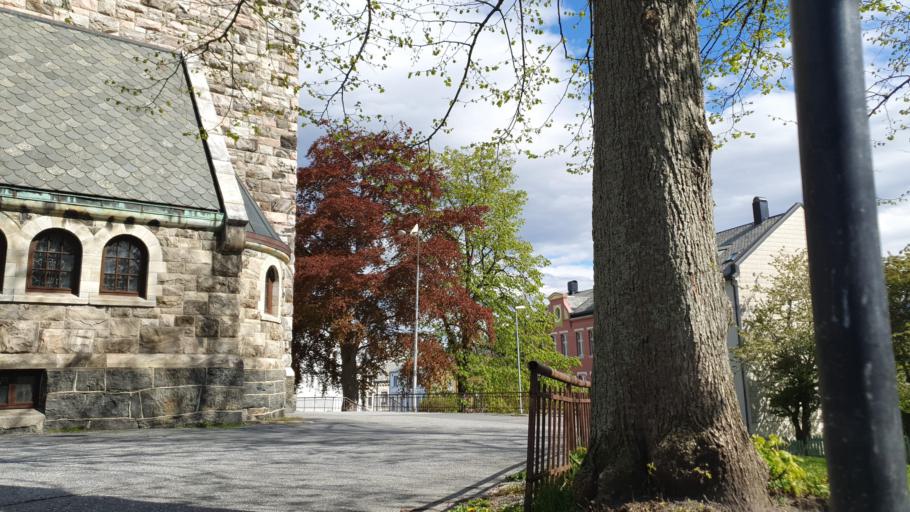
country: NO
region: More og Romsdal
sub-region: Alesund
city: Alesund
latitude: 62.4710
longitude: 6.1450
